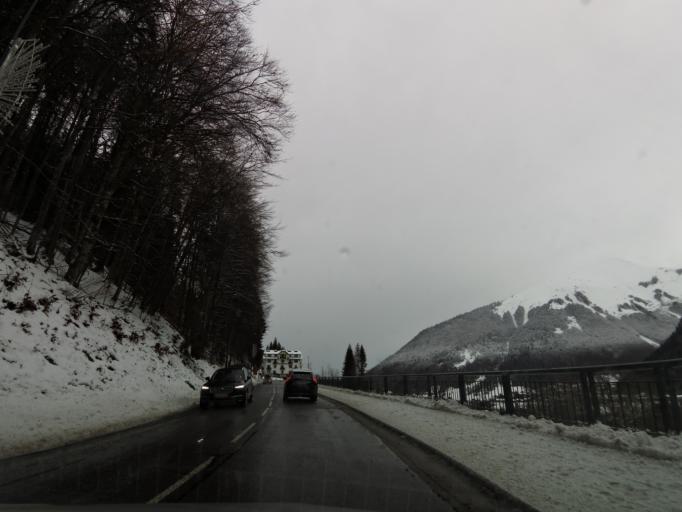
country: FR
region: Rhone-Alpes
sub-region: Departement de la Haute-Savoie
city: Morzine
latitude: 46.1871
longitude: 6.6926
